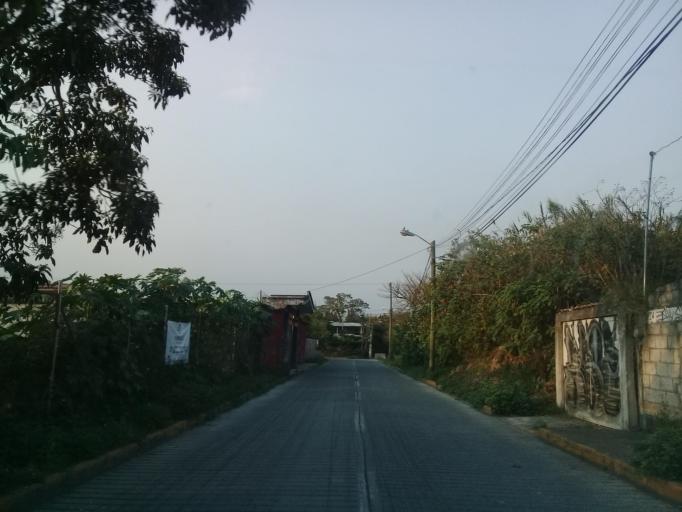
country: MX
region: Veracruz
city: Ixtac Zoquitlan
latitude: 18.8468
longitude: -97.0587
